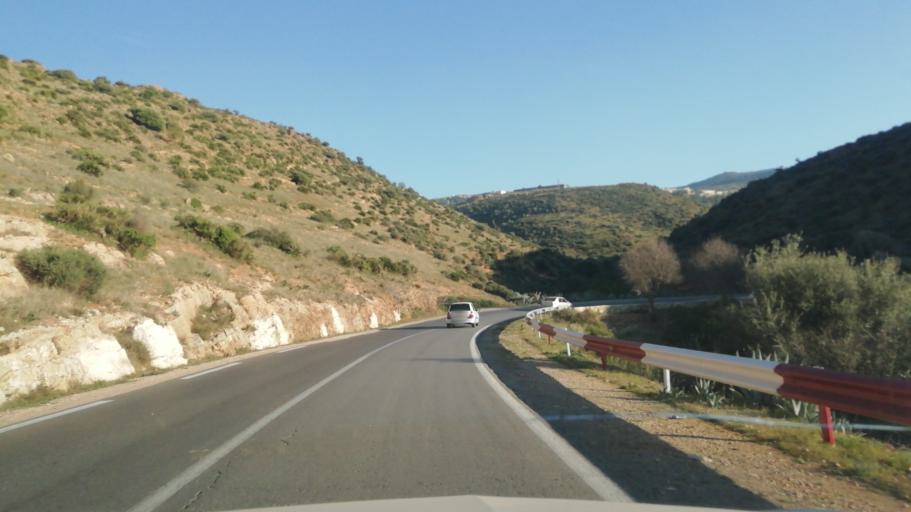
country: DZ
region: Tlemcen
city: Beni Mester
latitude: 34.8570
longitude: -1.4476
